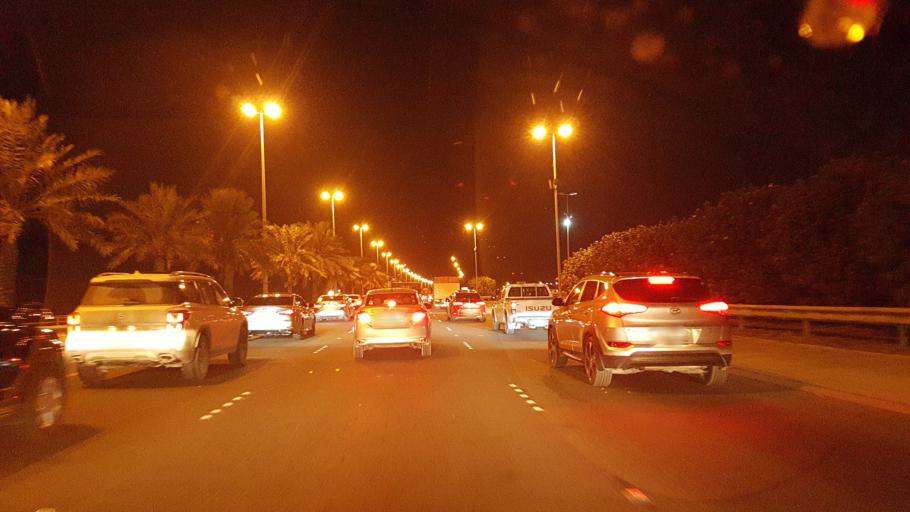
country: BH
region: Central Governorate
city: Madinat Hamad
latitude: 26.1583
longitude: 50.5056
